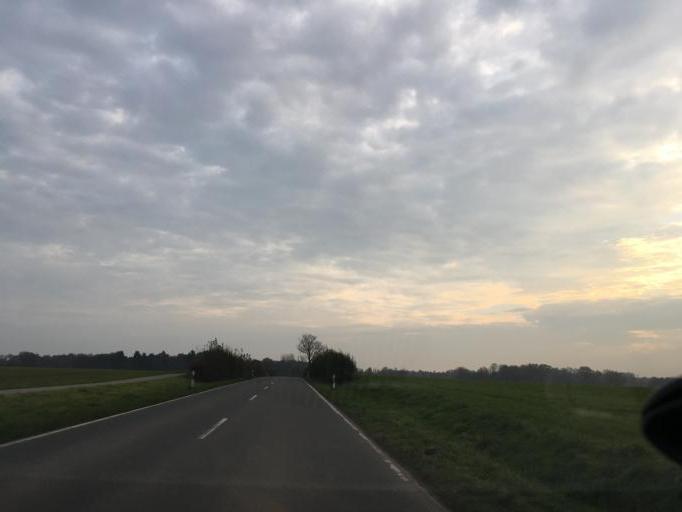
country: DE
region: Lower Saxony
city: Bergen
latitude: 52.8244
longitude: 9.9712
